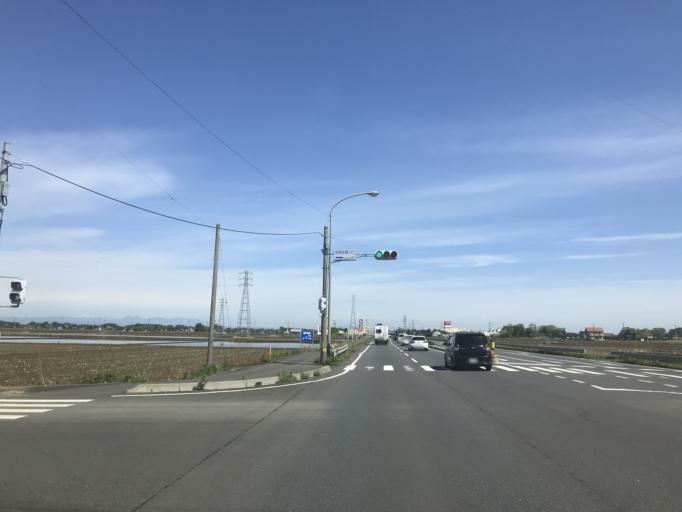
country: JP
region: Ibaraki
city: Ishige
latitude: 36.1790
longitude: 139.9904
